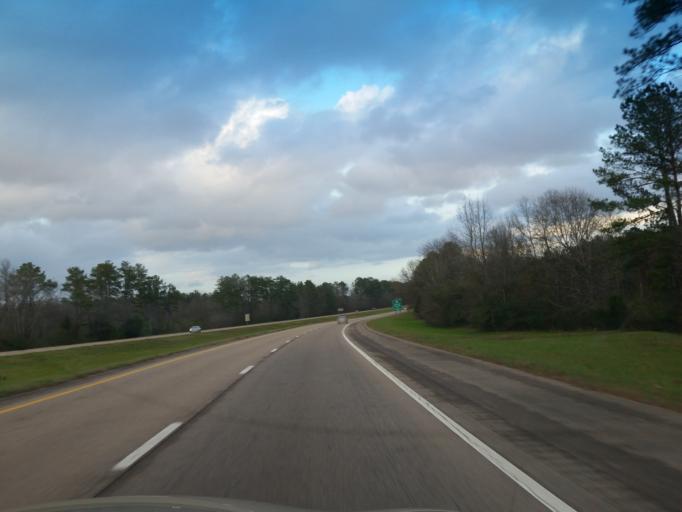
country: US
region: Mississippi
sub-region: Clarke County
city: Stonewall
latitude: 32.0450
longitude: -88.9193
